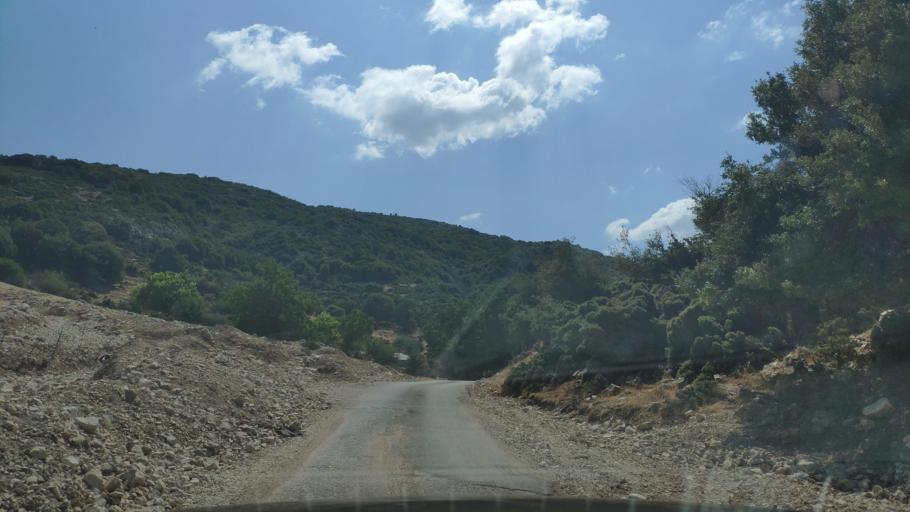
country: GR
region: West Greece
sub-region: Nomos Aitolias kai Akarnanias
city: Monastirakion
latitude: 38.8062
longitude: 20.9447
